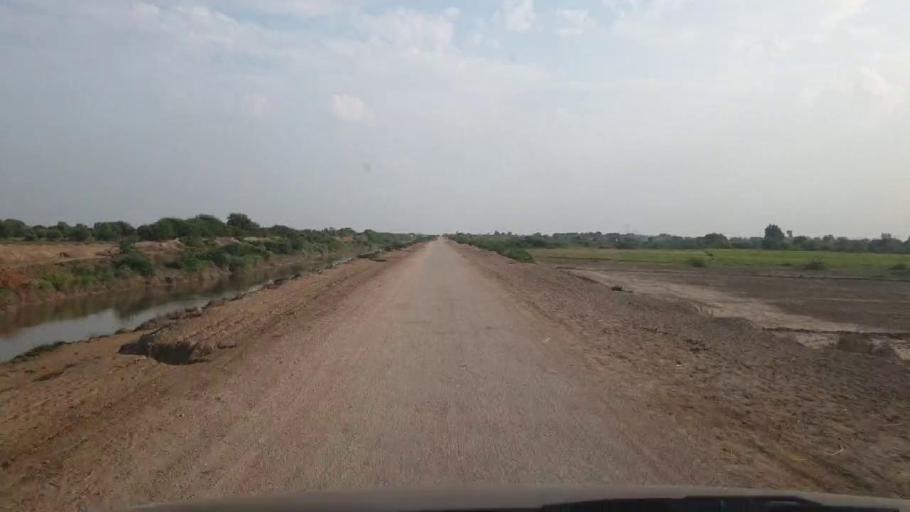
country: PK
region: Sindh
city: Badin
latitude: 24.5386
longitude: 68.6751
